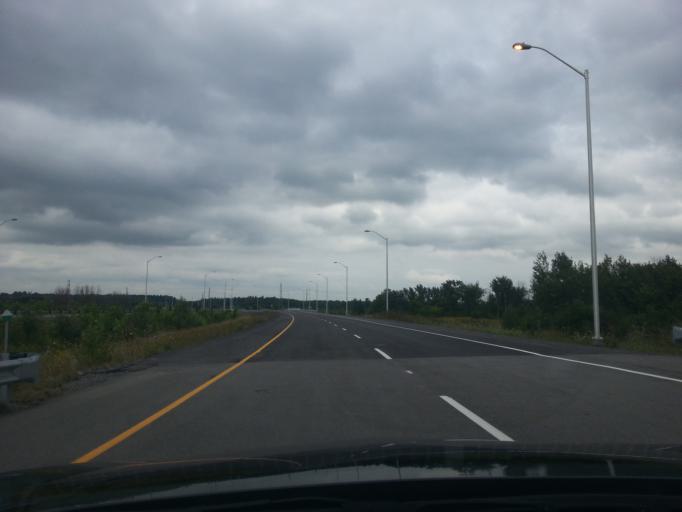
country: CA
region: Ontario
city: Ottawa
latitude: 45.3783
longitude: -75.5878
